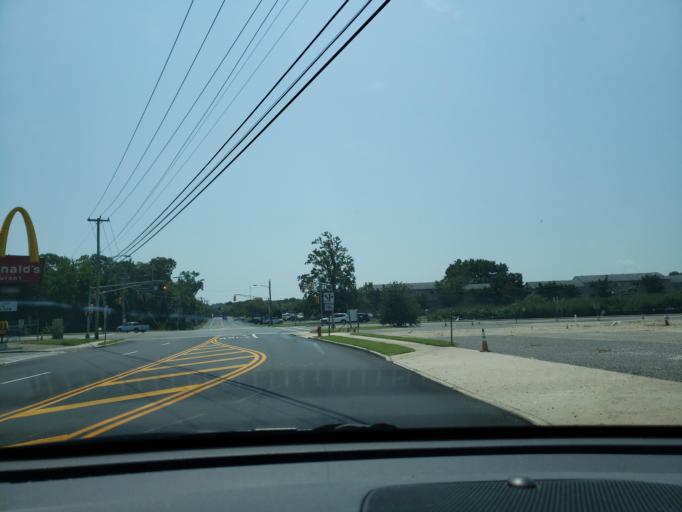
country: US
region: New Jersey
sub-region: Cape May County
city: North Cape May
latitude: 38.9739
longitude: -74.9425
